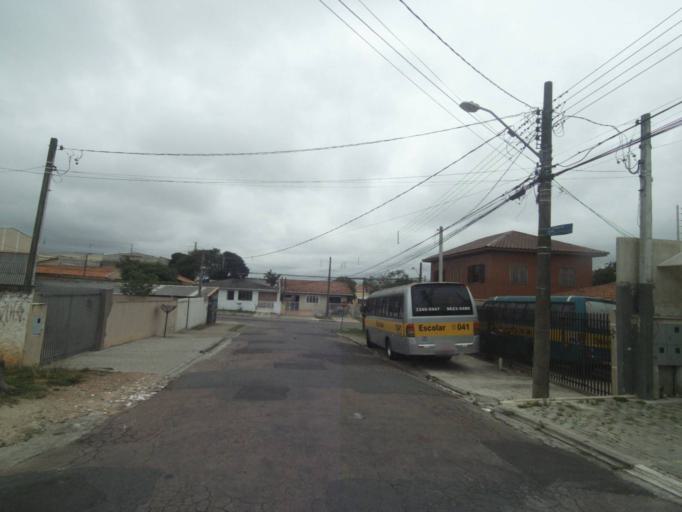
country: BR
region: Parana
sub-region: Sao Jose Dos Pinhais
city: Sao Jose dos Pinhais
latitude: -25.5401
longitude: -49.2813
